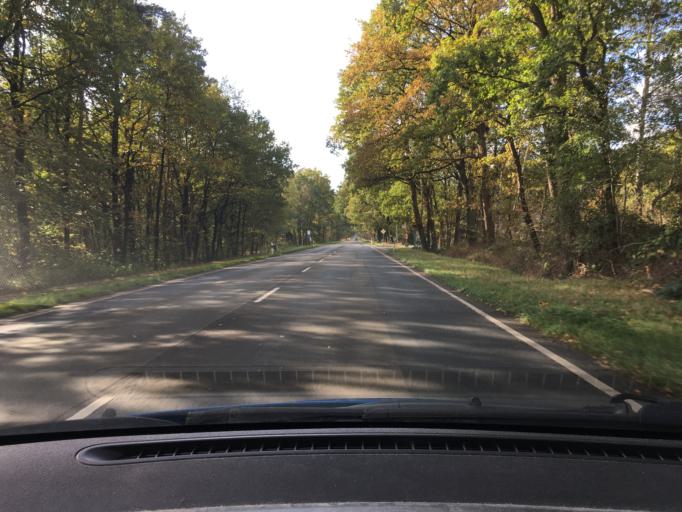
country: DE
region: Lower Saxony
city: Wistedt
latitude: 53.2650
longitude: 9.6710
